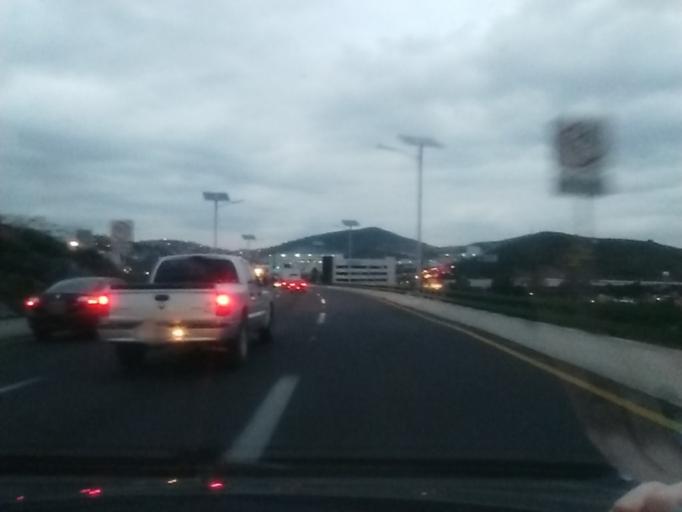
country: MX
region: Mexico
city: Tlalnepantla
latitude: 19.5638
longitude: -99.2066
